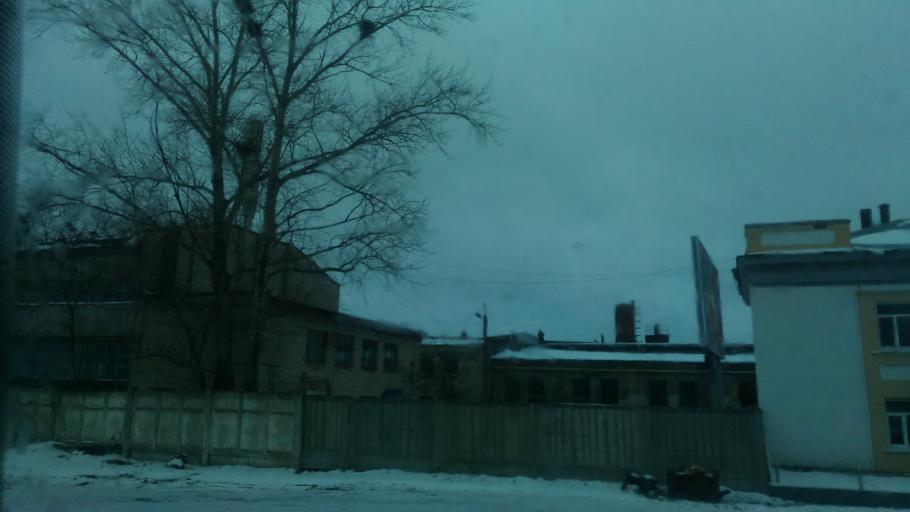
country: RU
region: Tula
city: Bolokhovo
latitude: 54.0631
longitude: 37.8013
